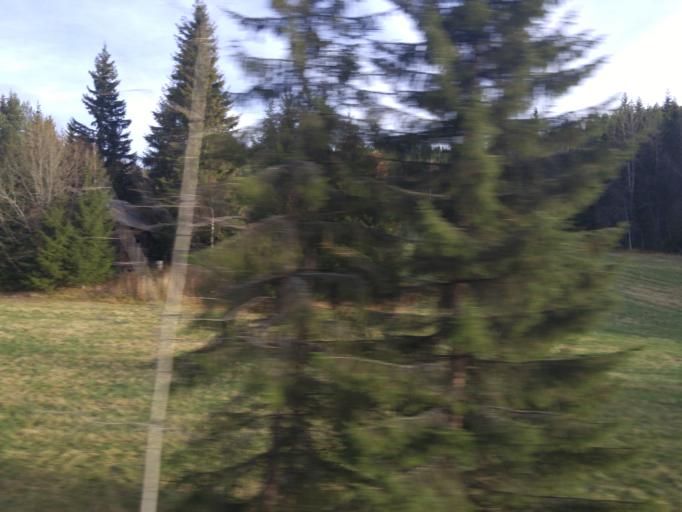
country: NO
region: Oppland
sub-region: Nord-Aurdal
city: Fagernes
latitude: 61.0579
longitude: 9.1639
